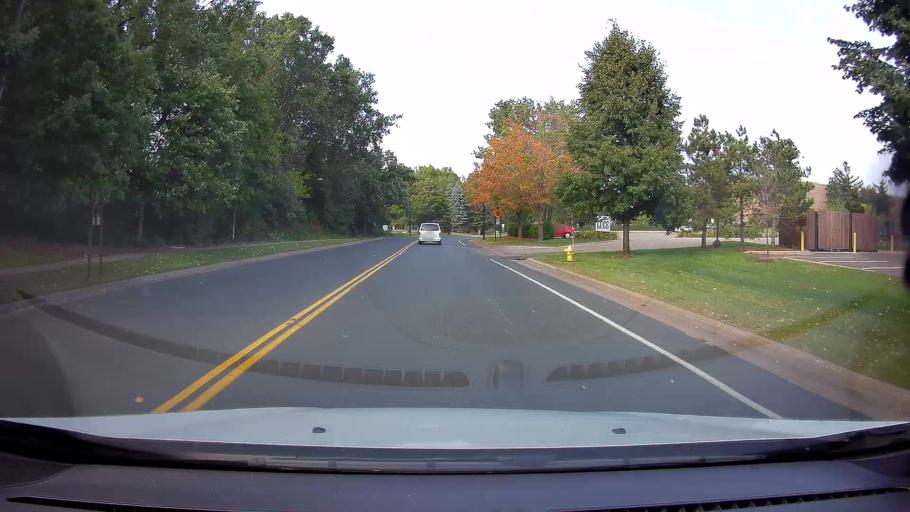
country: US
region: Minnesota
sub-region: Ramsey County
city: Roseville
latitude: 45.0266
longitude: -93.1691
